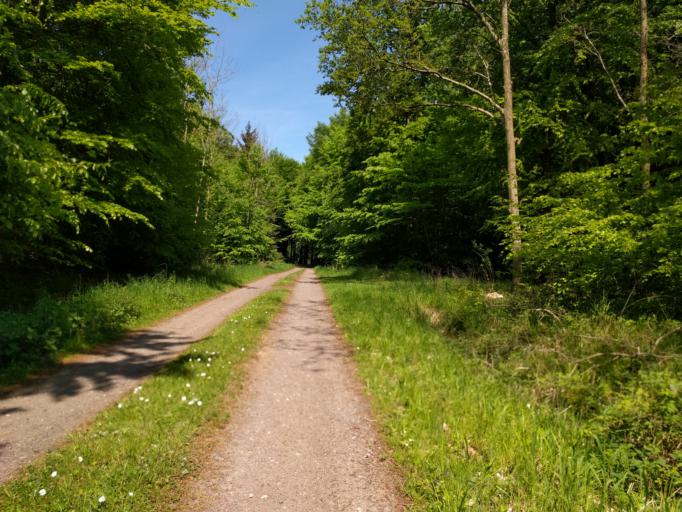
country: DK
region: Zealand
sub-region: Guldborgsund Kommune
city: Stubbekobing
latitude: 54.8369
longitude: 12.1346
